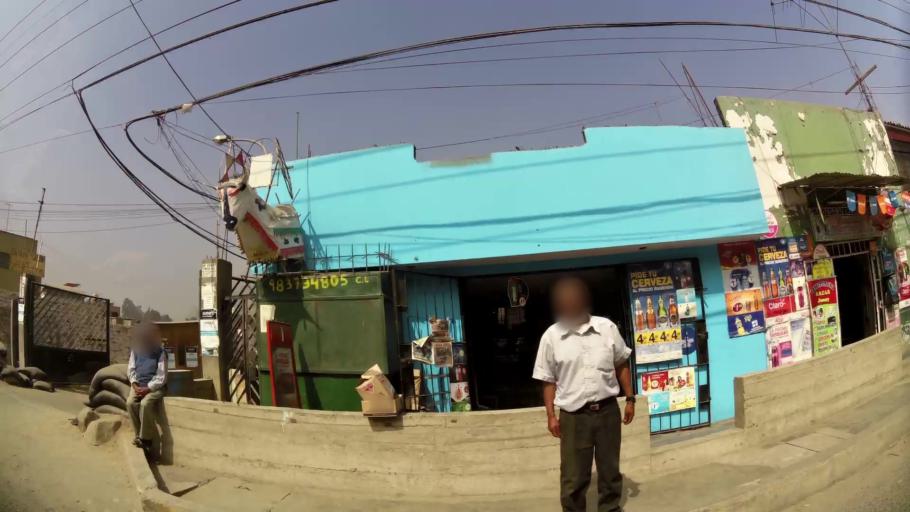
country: PE
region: Lima
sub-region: Provincia de Huarochiri
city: Ricardo Palma
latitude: -11.9230
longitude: -76.6790
